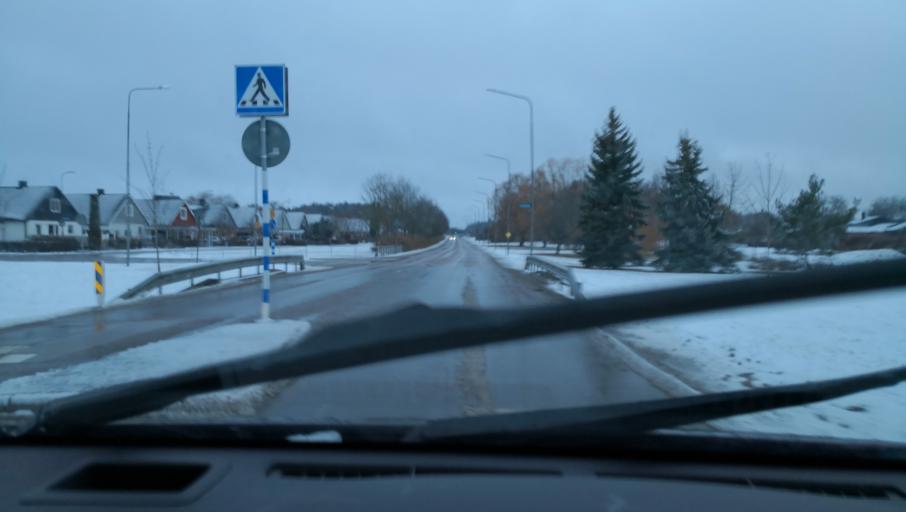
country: SE
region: Vaestmanland
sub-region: Kopings Kommun
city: Koping
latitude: 59.5167
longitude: 16.0118
